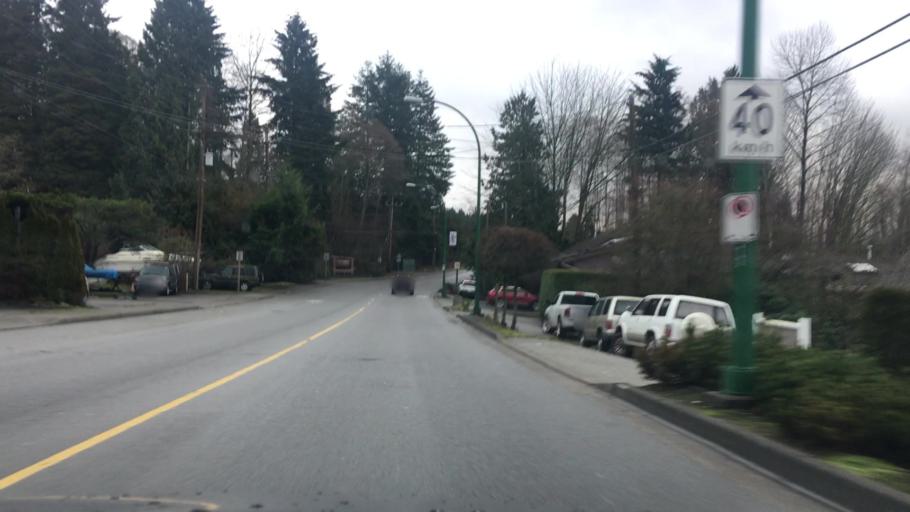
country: CA
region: British Columbia
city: Burnaby
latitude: 49.3088
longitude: -122.9927
